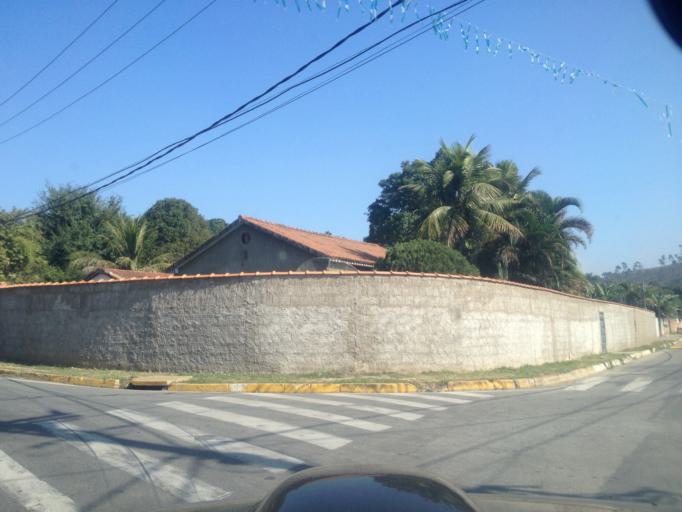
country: BR
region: Rio de Janeiro
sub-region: Porto Real
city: Porto Real
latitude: -22.4430
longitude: -44.3160
